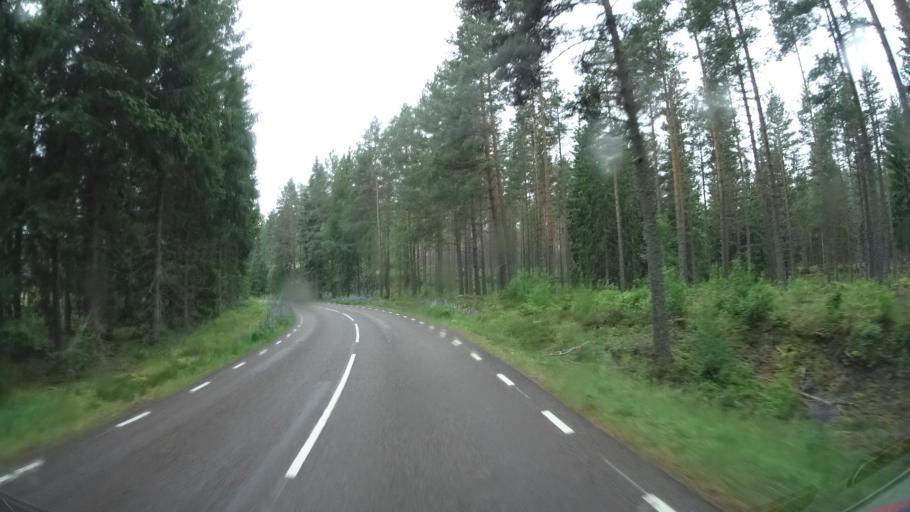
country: SE
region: Joenkoeping
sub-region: Eksjo Kommun
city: Mariannelund
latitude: 57.6461
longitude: 15.5975
